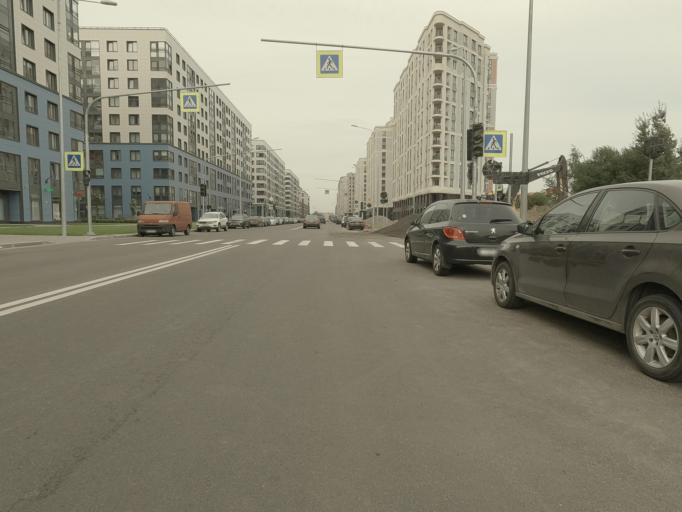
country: RU
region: St.-Petersburg
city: Admiralteisky
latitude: 59.8980
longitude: 30.3121
